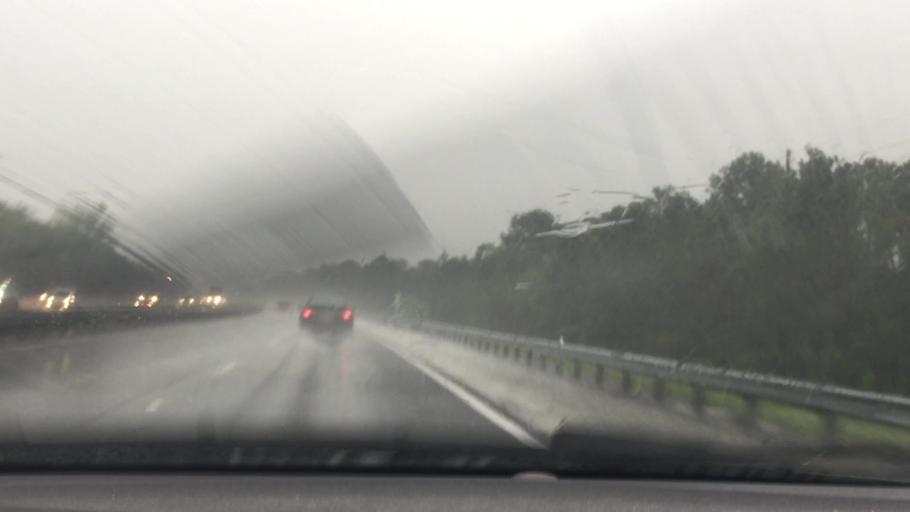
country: US
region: Florida
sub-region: Osceola County
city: Buenaventura Lakes
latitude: 28.3124
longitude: -81.3679
